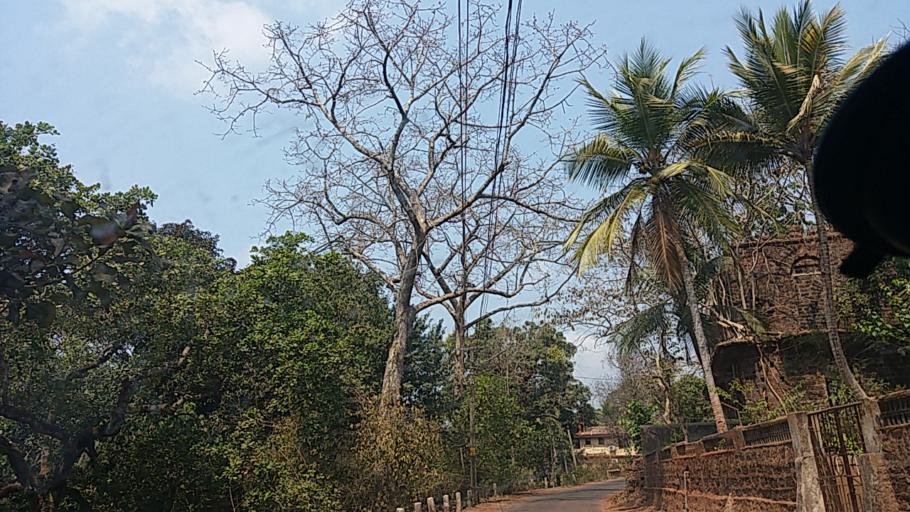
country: IN
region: Goa
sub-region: South Goa
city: Sancoale
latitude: 15.3742
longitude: 73.9145
